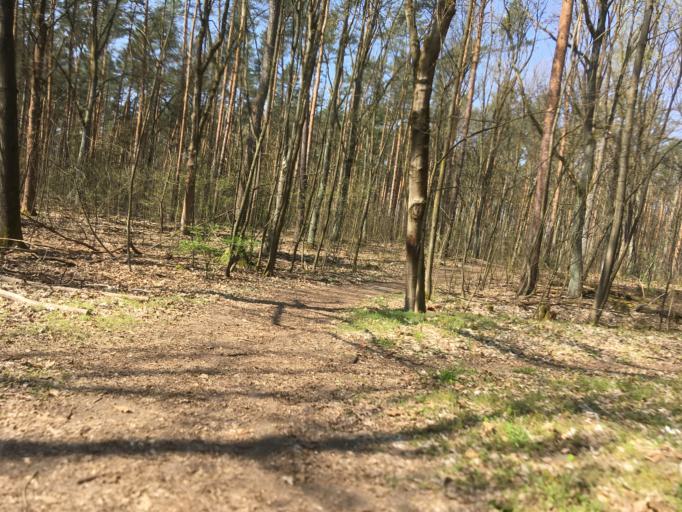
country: DE
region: Berlin
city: Grunewald
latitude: 52.4757
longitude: 13.2344
